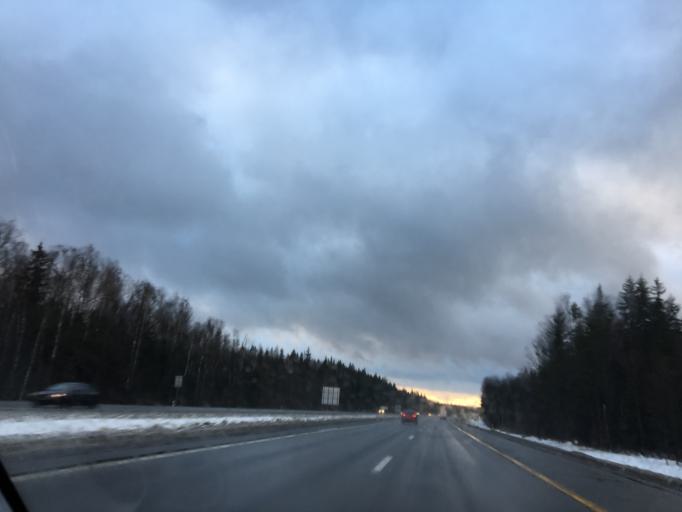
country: RU
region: Moskovskaya
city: Novyy Byt
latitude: 55.0251
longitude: 37.5579
